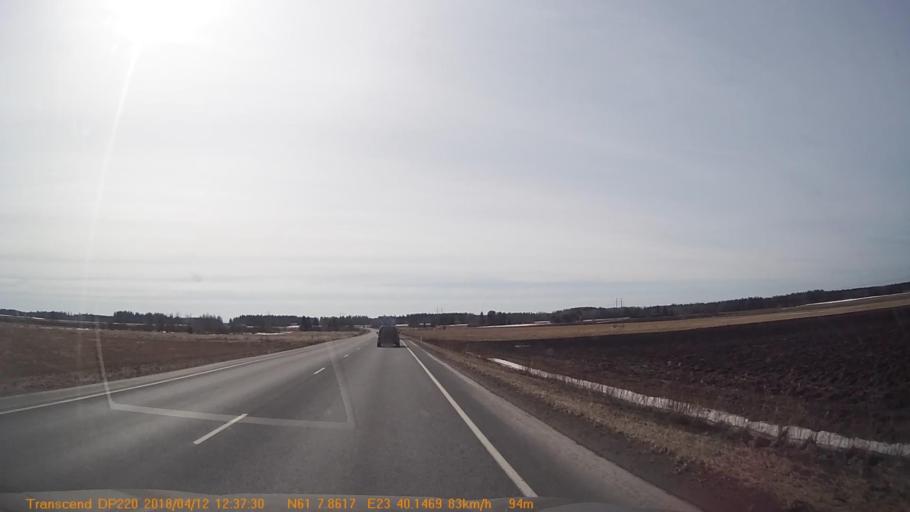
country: FI
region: Pirkanmaa
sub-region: Etelae-Pirkanmaa
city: Kylmaekoski
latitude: 61.1309
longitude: 23.6697
